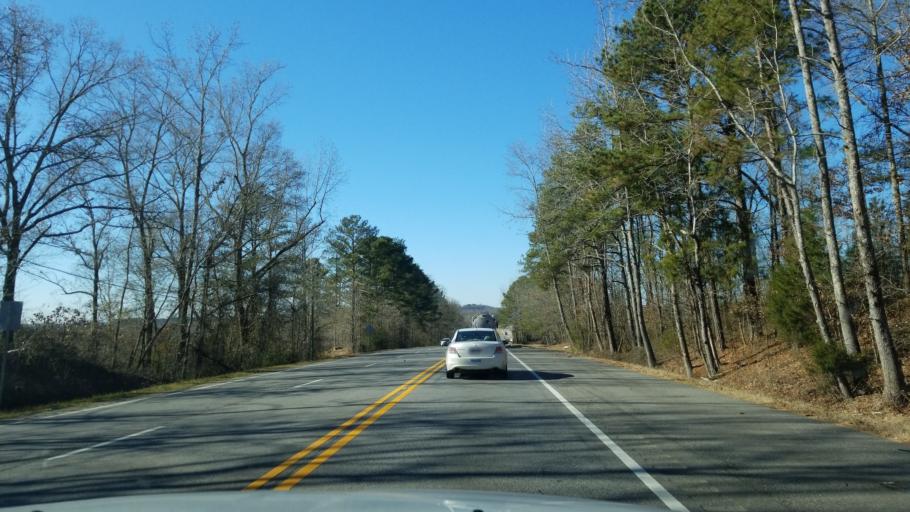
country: US
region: Alabama
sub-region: Pickens County
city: Gordo
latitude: 33.3327
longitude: -87.9187
